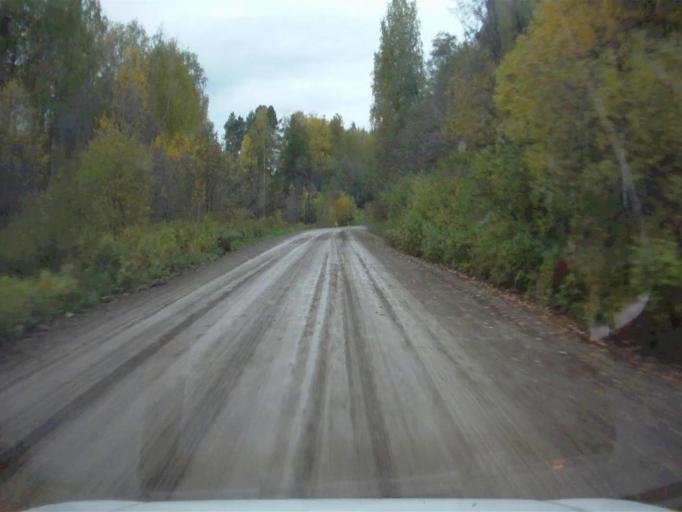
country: RU
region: Chelyabinsk
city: Nyazepetrovsk
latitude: 56.1006
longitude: 59.3899
